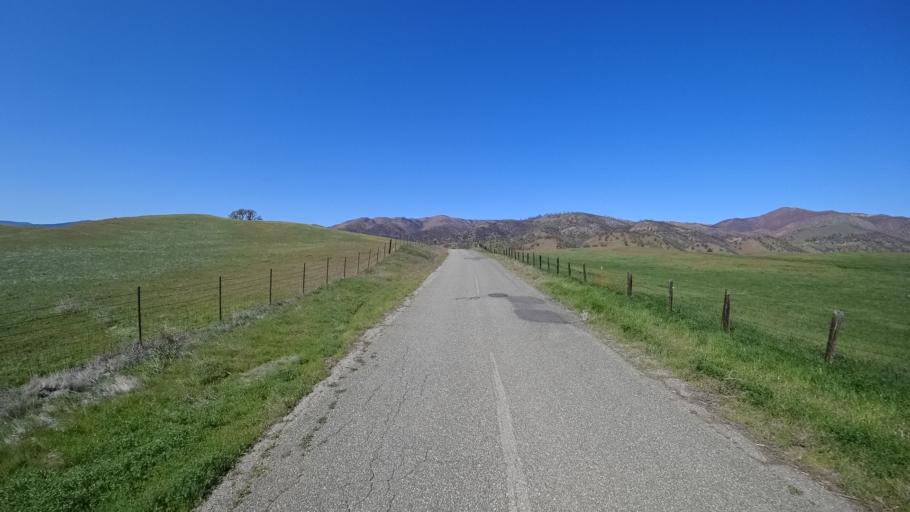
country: US
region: California
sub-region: Tehama County
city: Rancho Tehama Reserve
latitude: 39.6993
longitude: -122.5589
